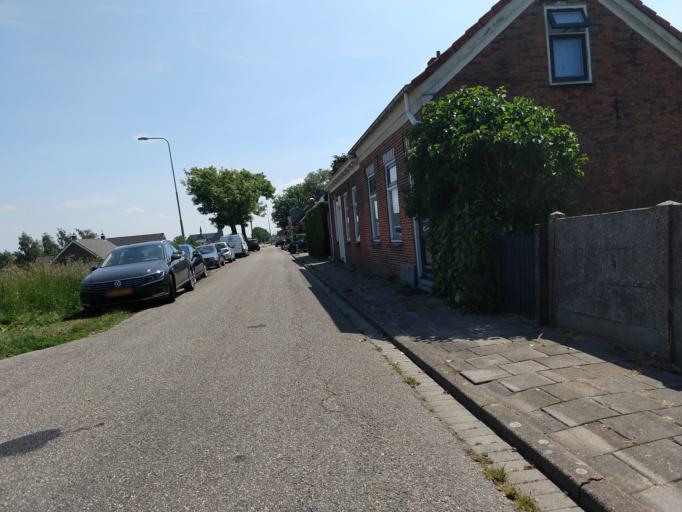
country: NL
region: Zeeland
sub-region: Gemeente Borsele
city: Borssele
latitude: 51.4603
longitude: 3.7671
